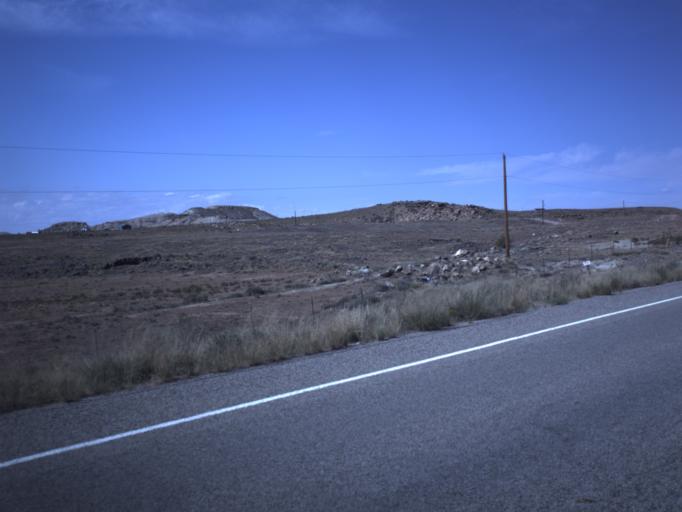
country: US
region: Colorado
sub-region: Montezuma County
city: Towaoc
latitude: 37.1627
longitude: -109.0707
